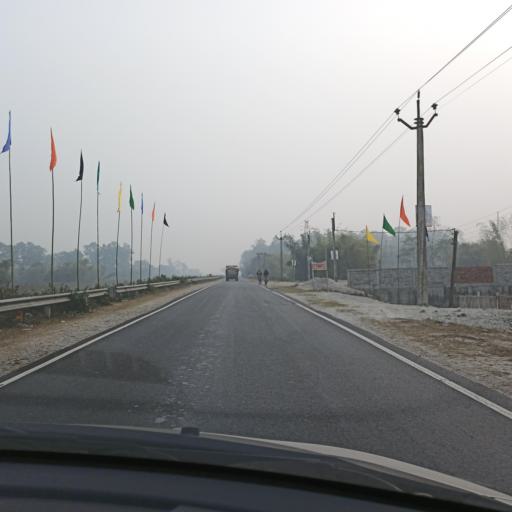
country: IN
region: West Bengal
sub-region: Darjiling
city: Shiliguri
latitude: 26.6770
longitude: 88.5413
